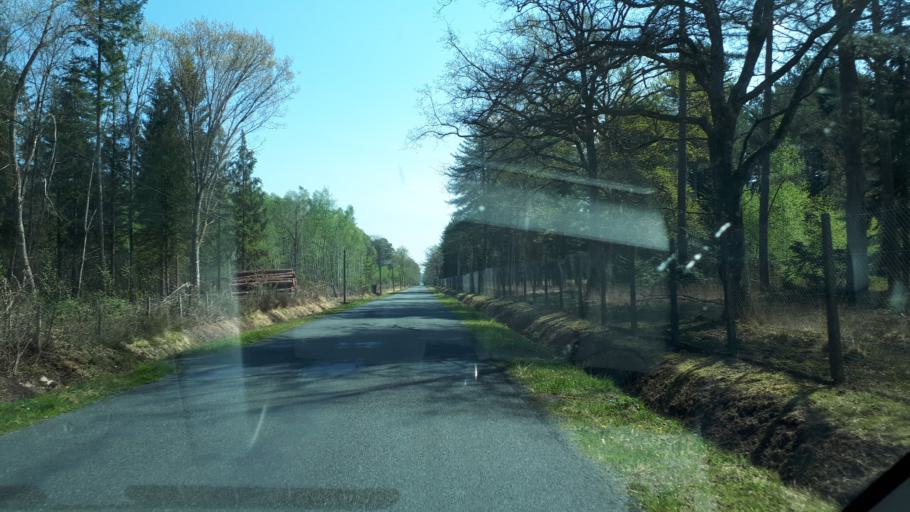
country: FR
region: Centre
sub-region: Departement du Cher
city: Neuvy-sur-Barangeon
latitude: 47.3178
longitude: 2.2262
